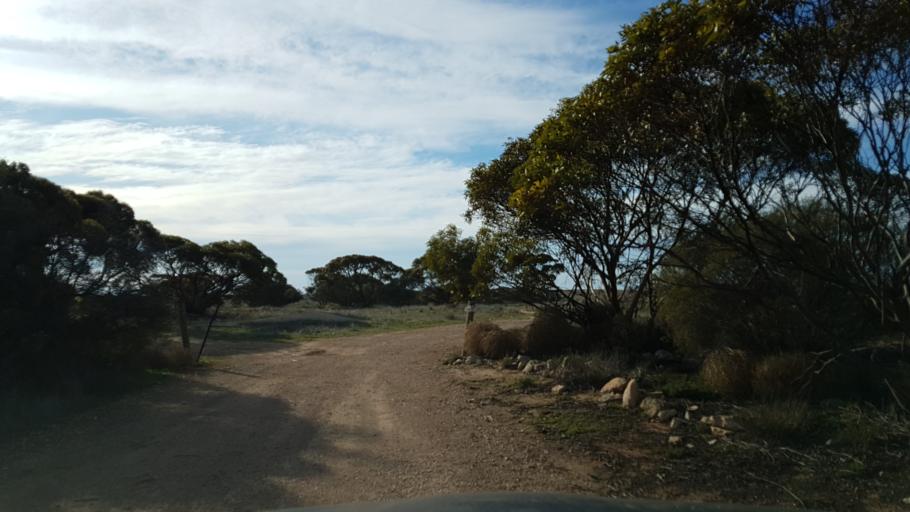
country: AU
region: South Australia
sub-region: Murray Bridge
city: Tailem Bend
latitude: -35.0635
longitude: 139.4655
